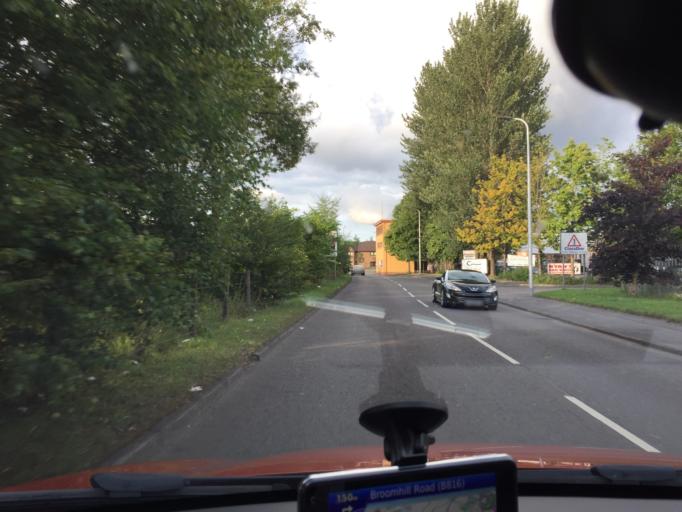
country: GB
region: Scotland
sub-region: Falkirk
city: Bonnybridge
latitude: 55.9983
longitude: -3.8886
